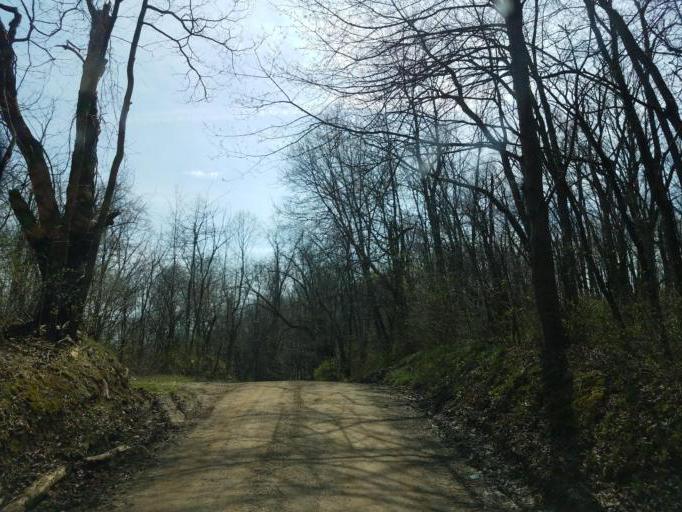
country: US
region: Ohio
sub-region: Knox County
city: Oak Hill
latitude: 40.3808
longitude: -82.1636
